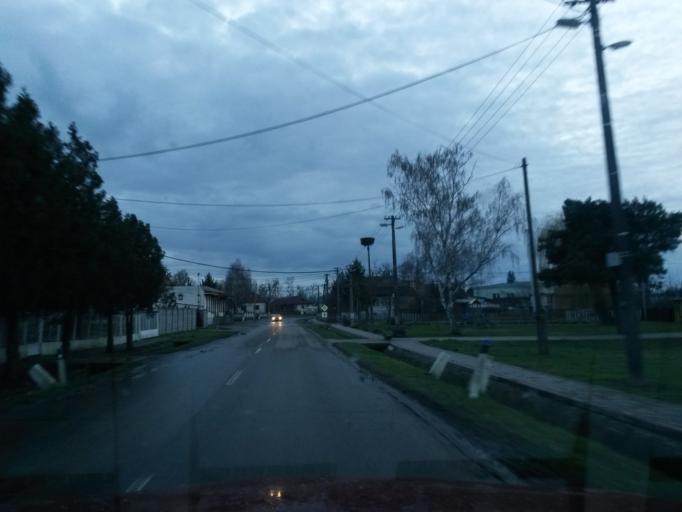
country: HU
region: Borsod-Abauj-Zemplen
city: Ricse
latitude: 48.4765
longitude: 21.9056
